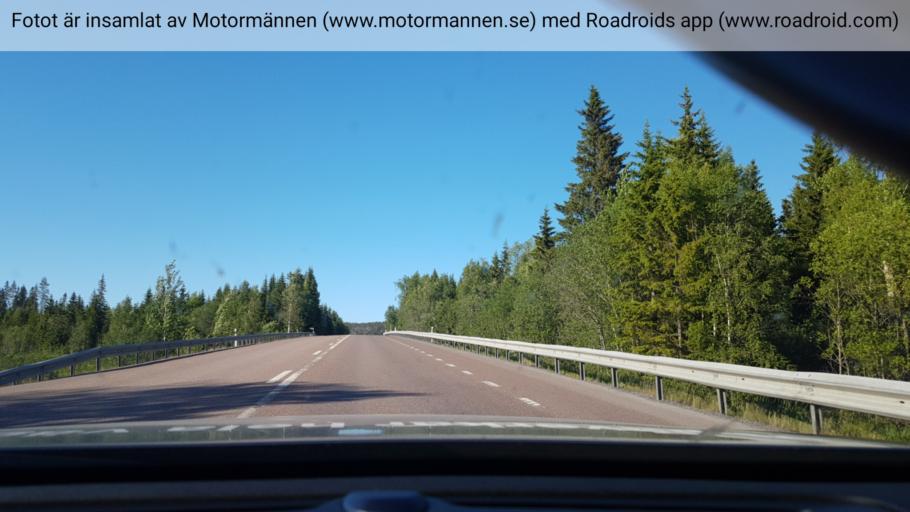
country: SE
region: Vaesternorrland
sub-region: Haernoesands Kommun
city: Haernoesand
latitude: 62.6978
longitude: 17.8545
